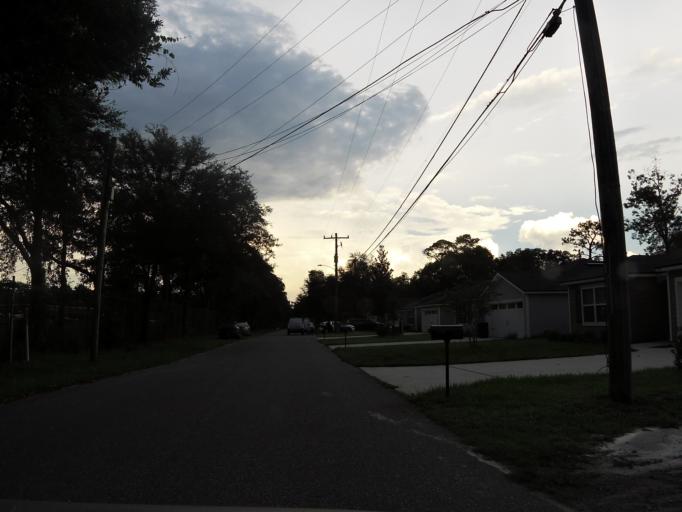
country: US
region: Florida
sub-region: Duval County
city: Jacksonville
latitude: 30.3194
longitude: -81.7786
